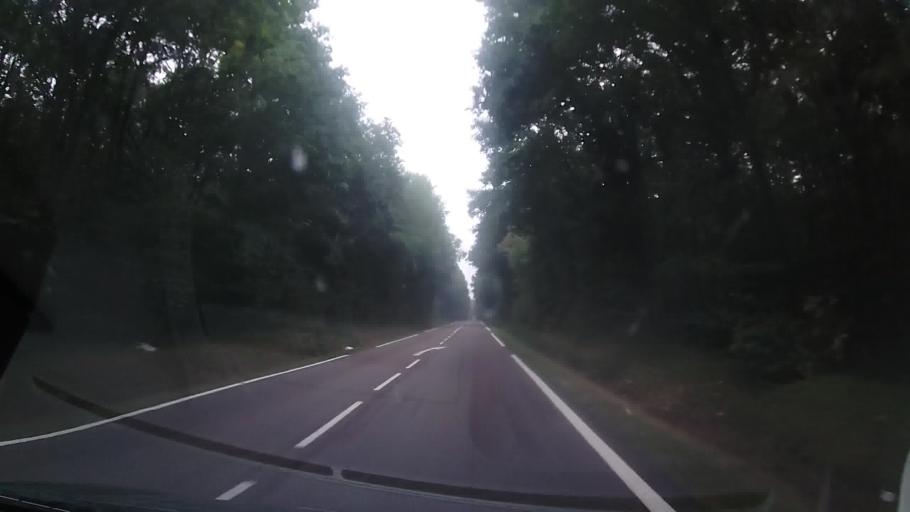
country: FR
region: Ile-de-France
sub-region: Departement de l'Essonne
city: Dourdan
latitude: 48.5543
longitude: 1.9800
